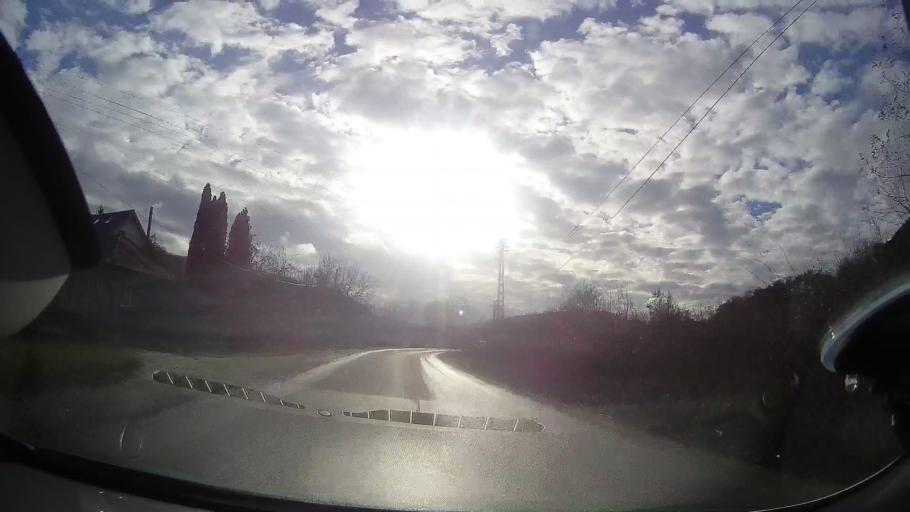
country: RO
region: Cluj
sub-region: Comuna Savadisla
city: Savadisla
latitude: 46.6789
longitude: 23.4563
